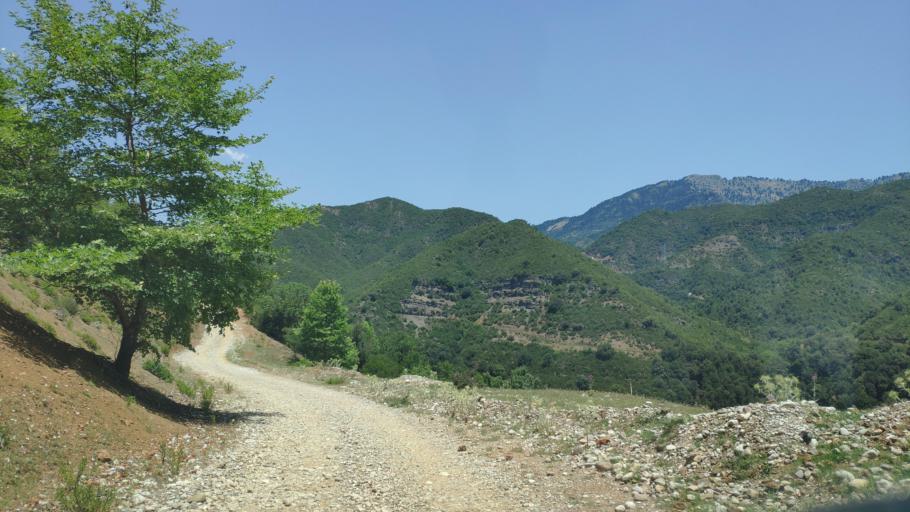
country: GR
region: Thessaly
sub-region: Nomos Kardhitsas
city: Anthiro
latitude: 39.1769
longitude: 21.3699
